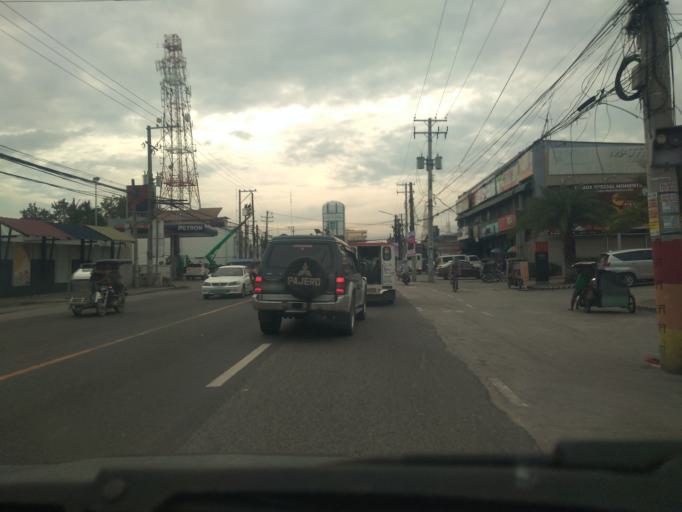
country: PH
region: Central Luzon
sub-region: Province of Pampanga
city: San Fernando
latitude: 15.0342
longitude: 120.6865
